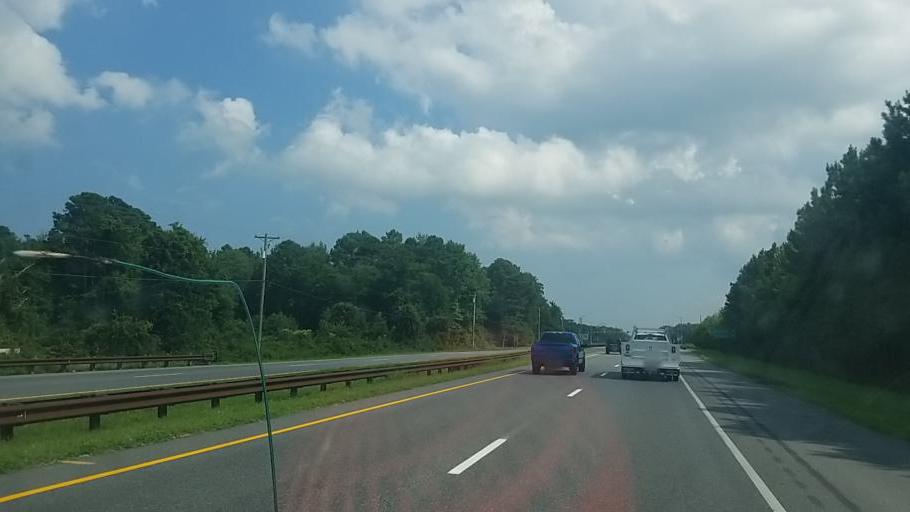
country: US
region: Delaware
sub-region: Sussex County
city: Selbyville
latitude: 38.4436
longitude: -75.2282
